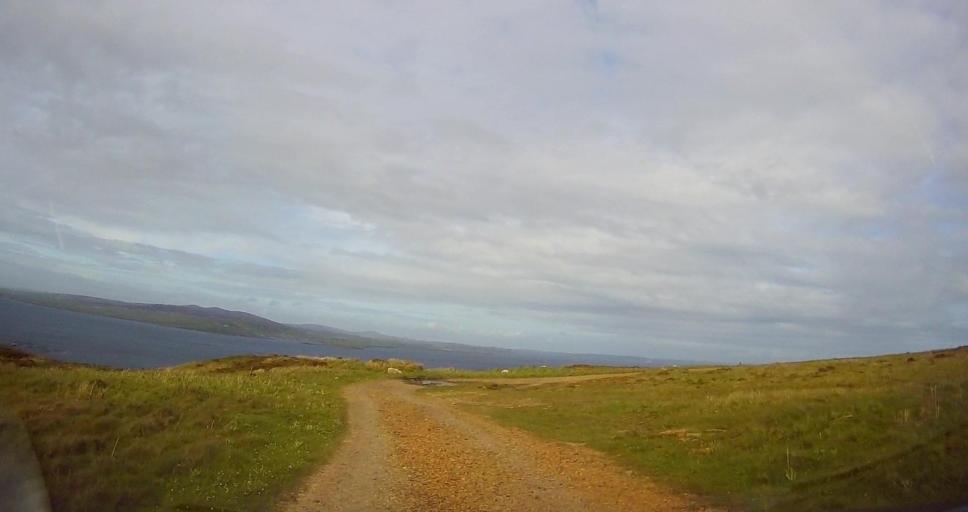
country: GB
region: Scotland
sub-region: Orkney Islands
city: Stromness
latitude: 58.8793
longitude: -3.2440
